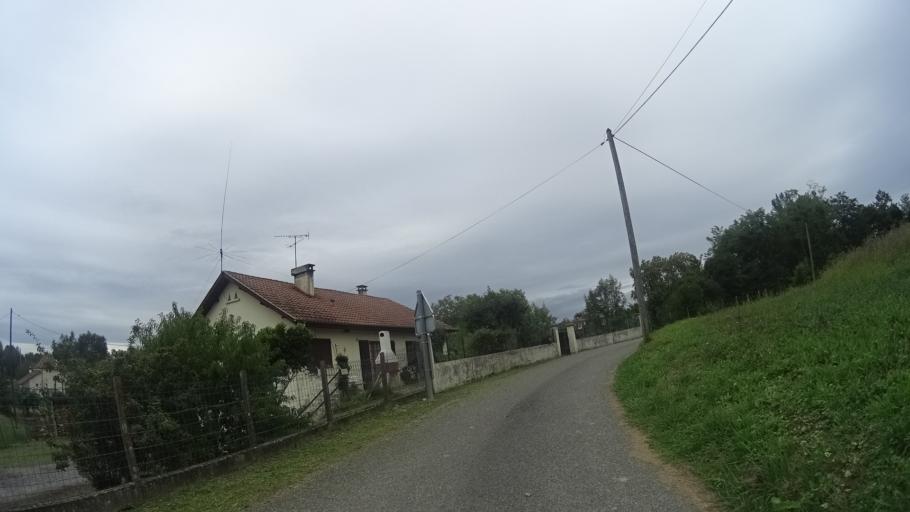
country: FR
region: Aquitaine
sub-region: Departement des Pyrenees-Atlantiques
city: Orthez
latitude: 43.4710
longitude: -0.7245
